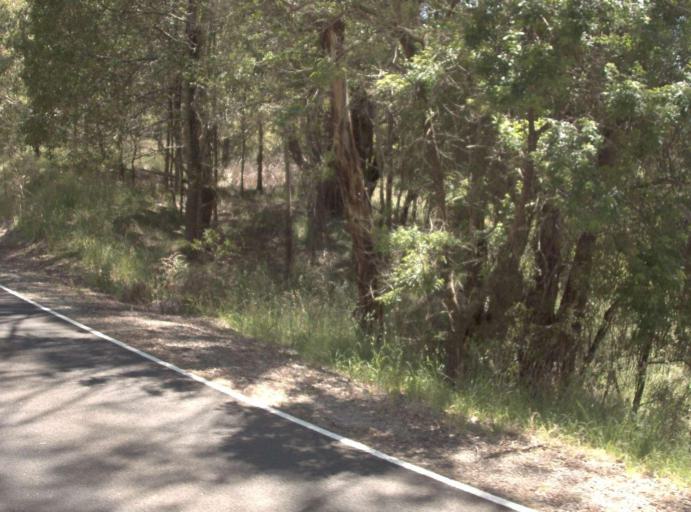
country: AU
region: Victoria
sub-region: East Gippsland
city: Lakes Entrance
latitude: -37.2416
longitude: 148.2557
